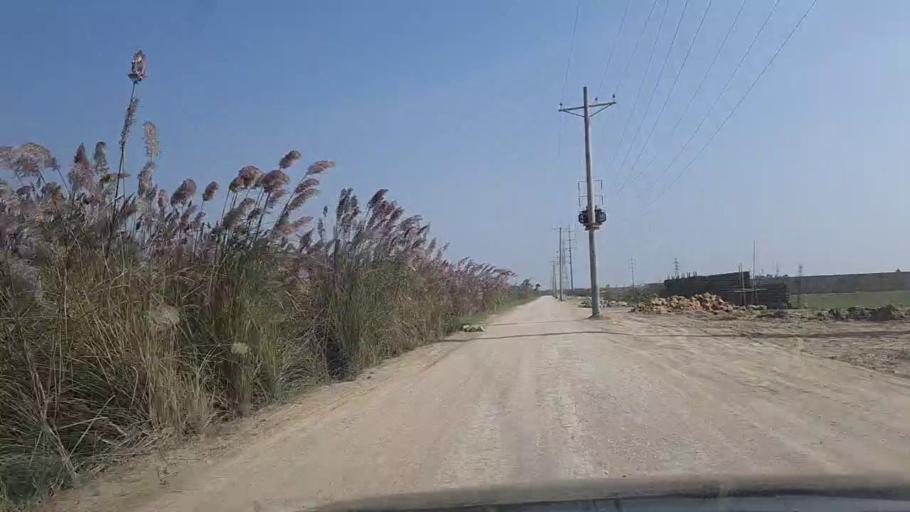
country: PK
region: Sindh
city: Gharo
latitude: 24.7219
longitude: 67.5481
